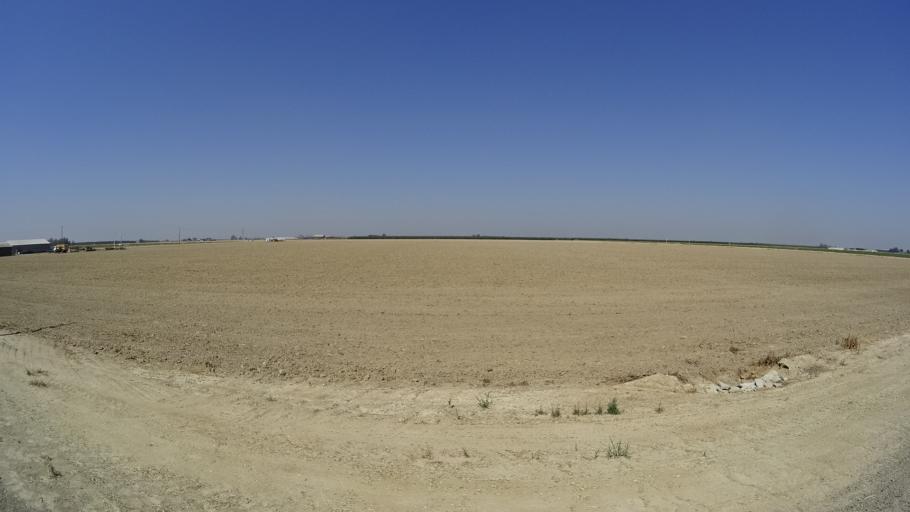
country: US
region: California
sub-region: Tulare County
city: Goshen
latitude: 36.3849
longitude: -119.5290
